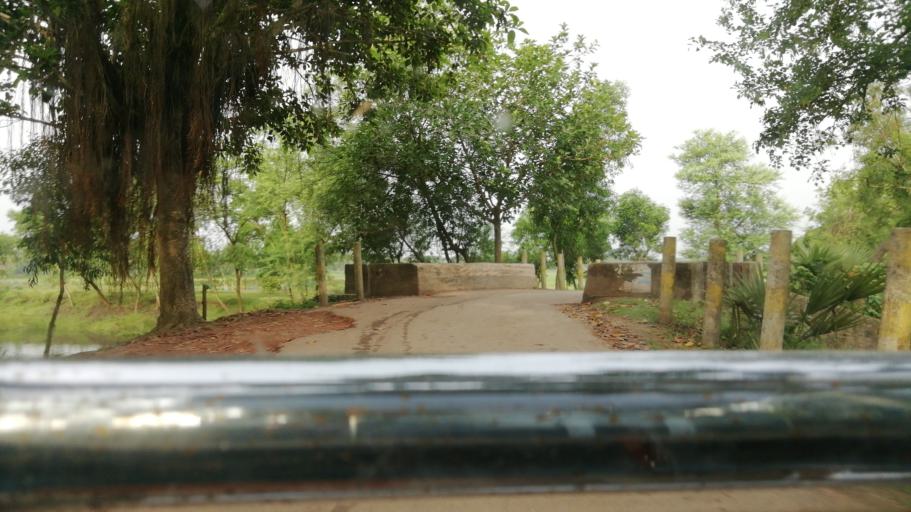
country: BD
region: Khulna
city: Bhatpara Abhaynagar
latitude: 23.0401
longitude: 89.3151
